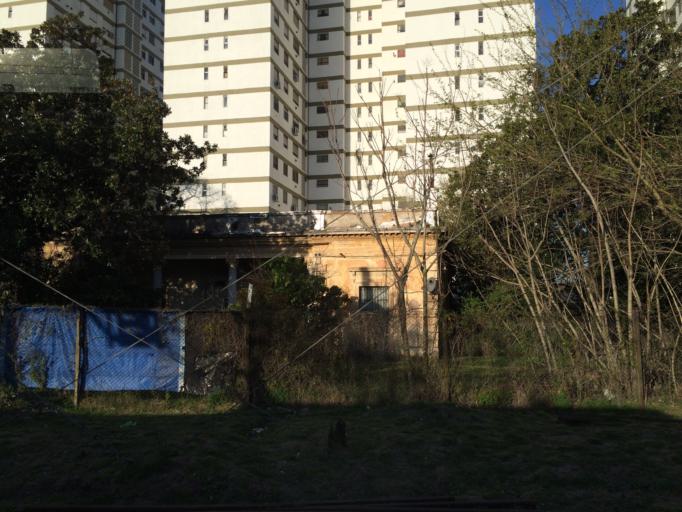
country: AR
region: Buenos Aires
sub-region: Partido de Lomas de Zamora
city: Lomas de Zamora
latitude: -34.7742
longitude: -58.3963
